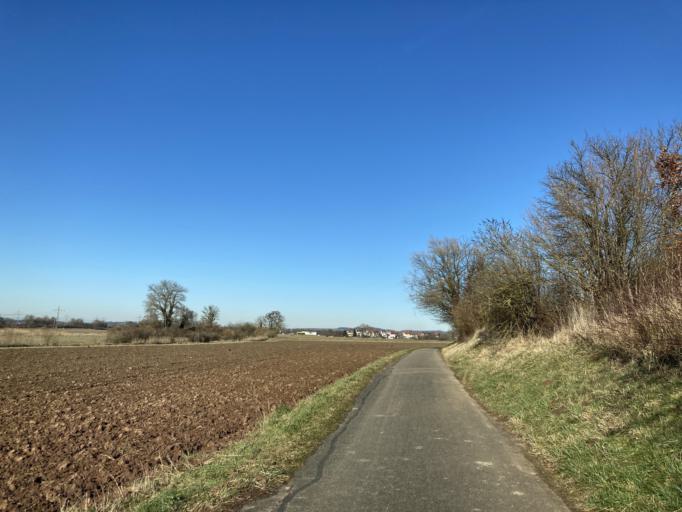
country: DE
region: Baden-Wuerttemberg
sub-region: Freiburg Region
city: Eichstetten
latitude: 48.0965
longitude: 7.7674
